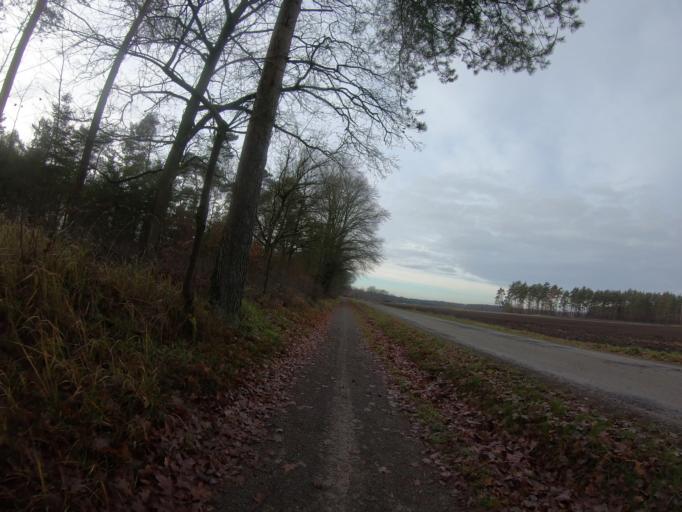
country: DE
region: Lower Saxony
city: Muden
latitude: 52.5100
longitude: 10.4162
